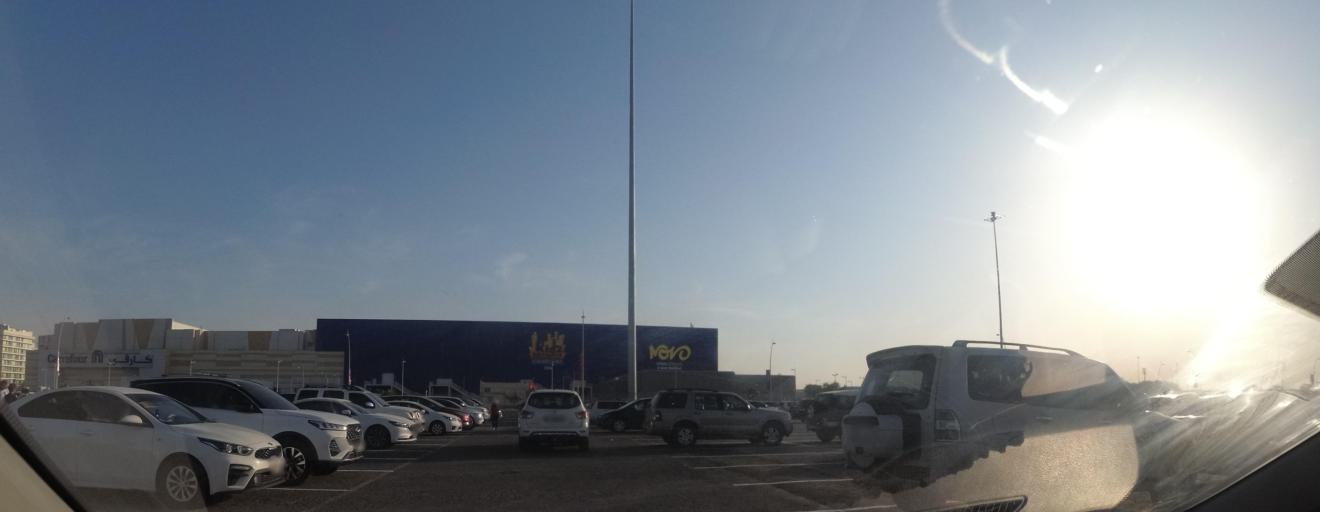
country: QA
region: Baladiyat ar Rayyan
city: Ar Rayyan
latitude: 25.3306
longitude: 51.3489
